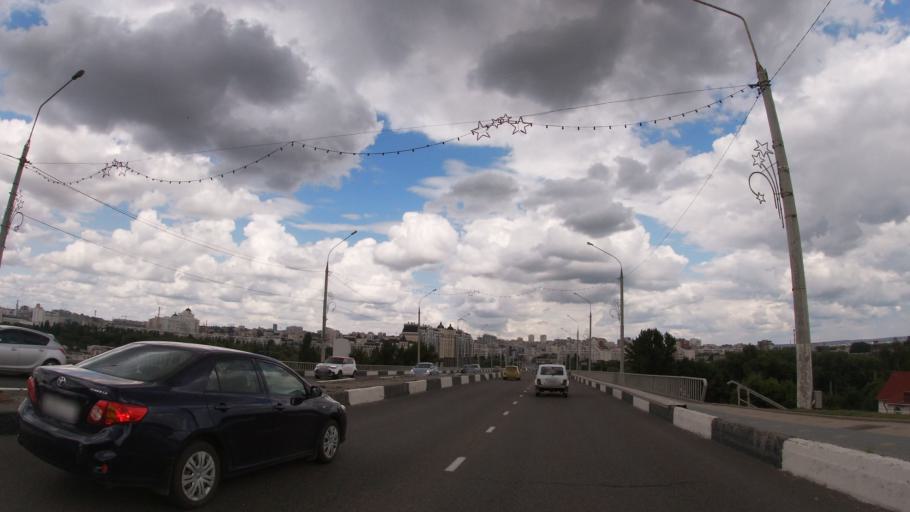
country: RU
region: Belgorod
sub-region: Belgorodskiy Rayon
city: Belgorod
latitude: 50.5851
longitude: 36.5864
